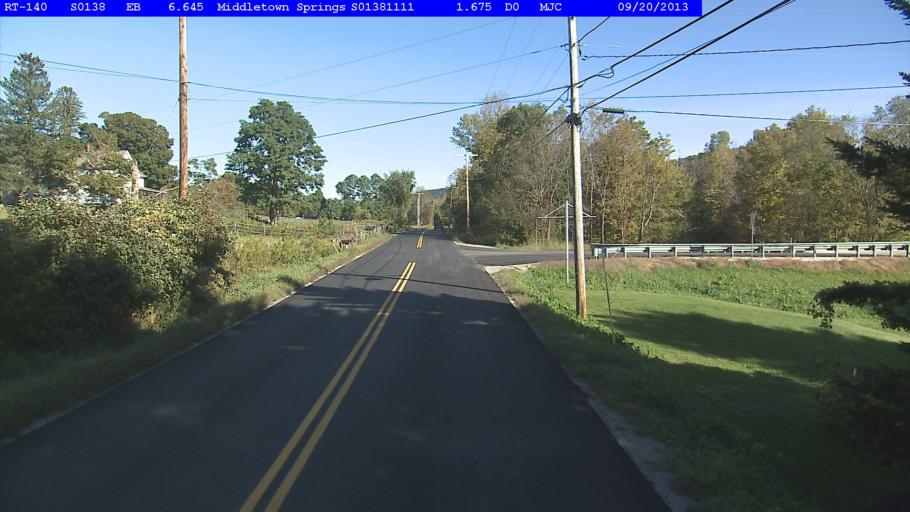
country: US
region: Vermont
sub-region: Rutland County
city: Poultney
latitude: 43.4844
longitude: -73.1481
